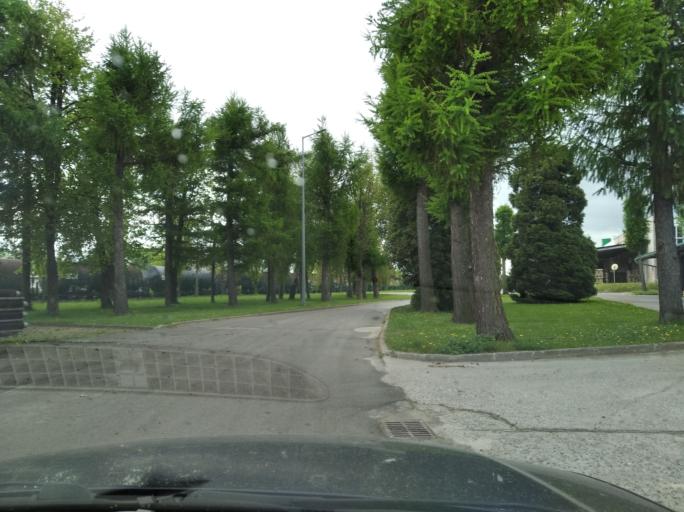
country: PL
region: Subcarpathian Voivodeship
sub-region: Powiat rzeszowski
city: Boguchwala
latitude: 49.9858
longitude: 21.9349
